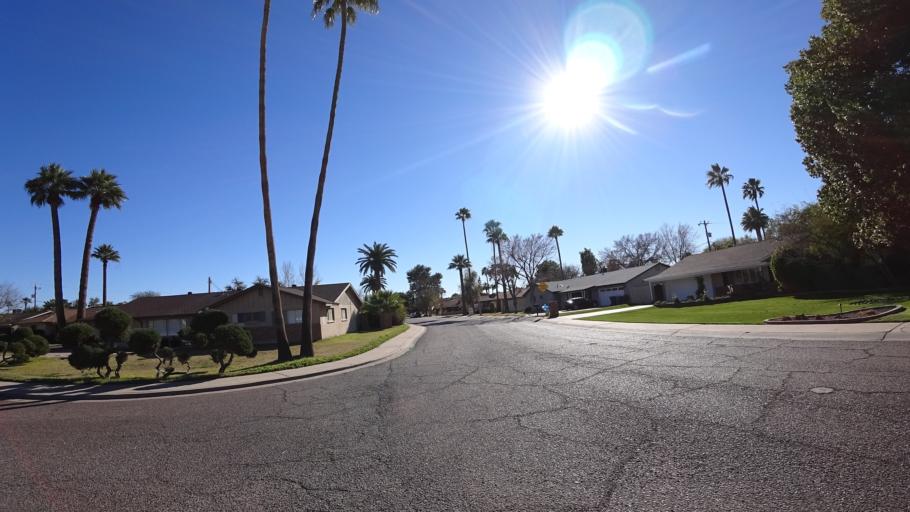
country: US
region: Arizona
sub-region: Maricopa County
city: Phoenix
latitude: 33.5517
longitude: -112.0668
